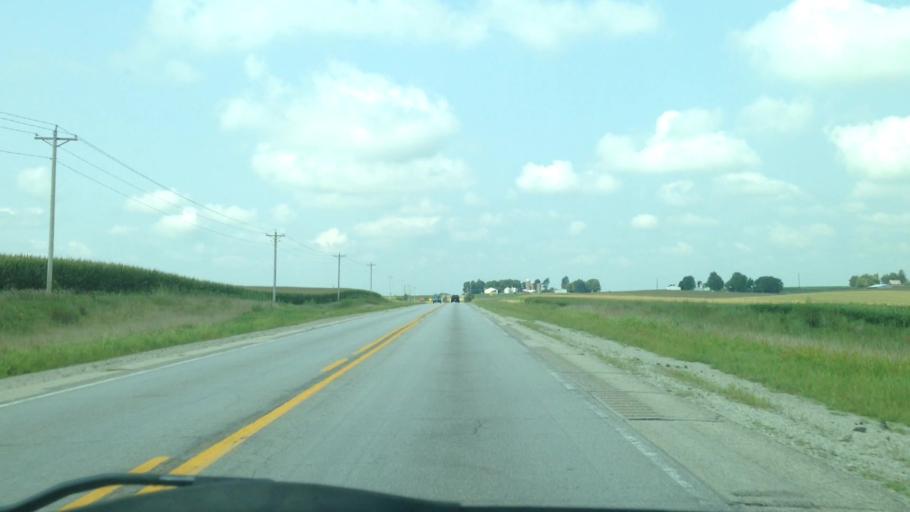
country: US
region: Iowa
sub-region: Benton County
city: Walford
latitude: 41.8762
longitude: -91.8574
